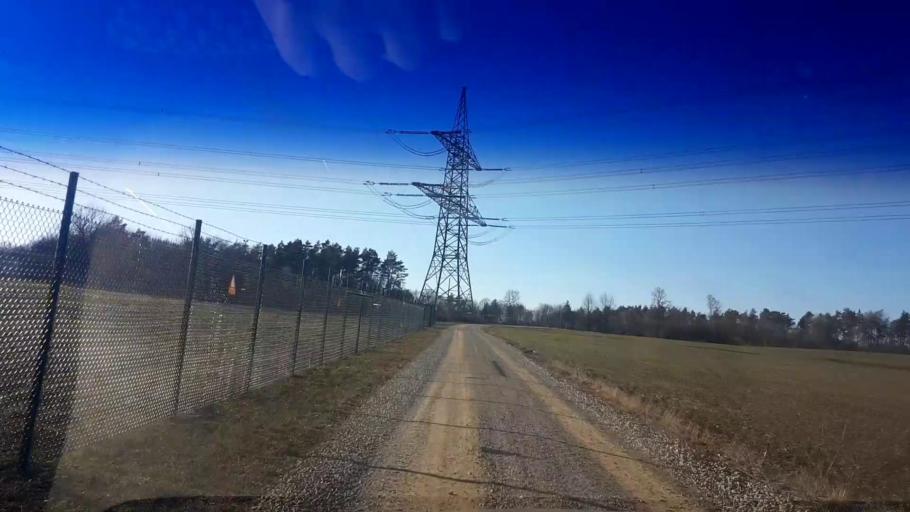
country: DE
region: Bavaria
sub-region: Upper Franconia
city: Poxdorf
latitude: 49.9806
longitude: 11.1050
